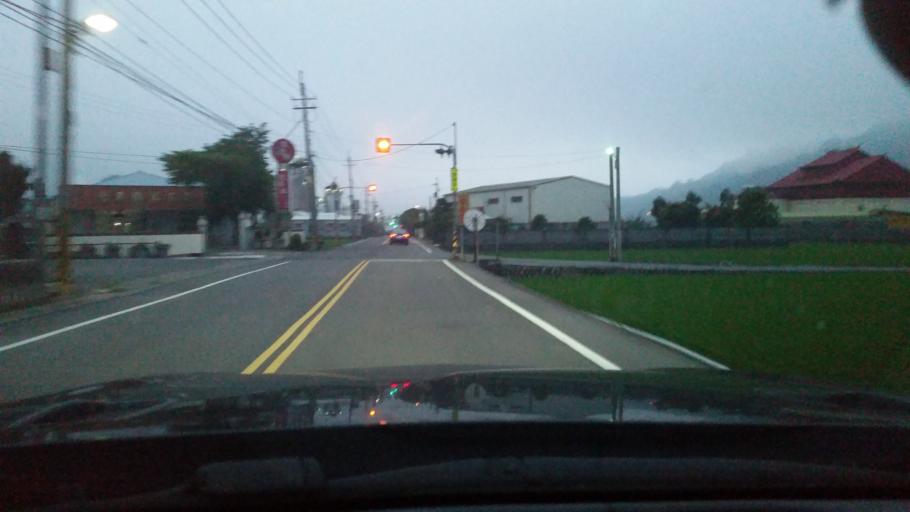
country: TW
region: Taiwan
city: Fengyuan
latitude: 24.3517
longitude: 120.7439
